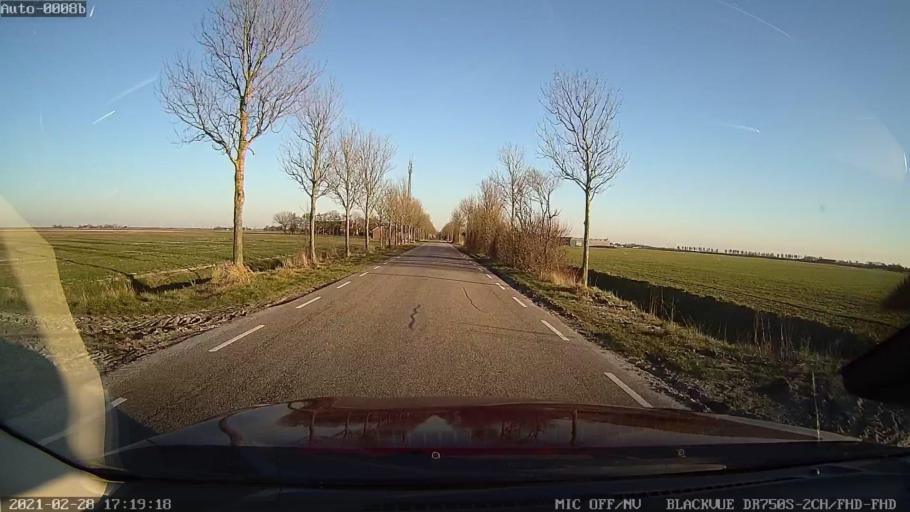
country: NL
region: South Holland
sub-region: Gemeente Goeree-Overflakkee
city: Ouddorp
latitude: 51.6974
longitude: 3.9683
